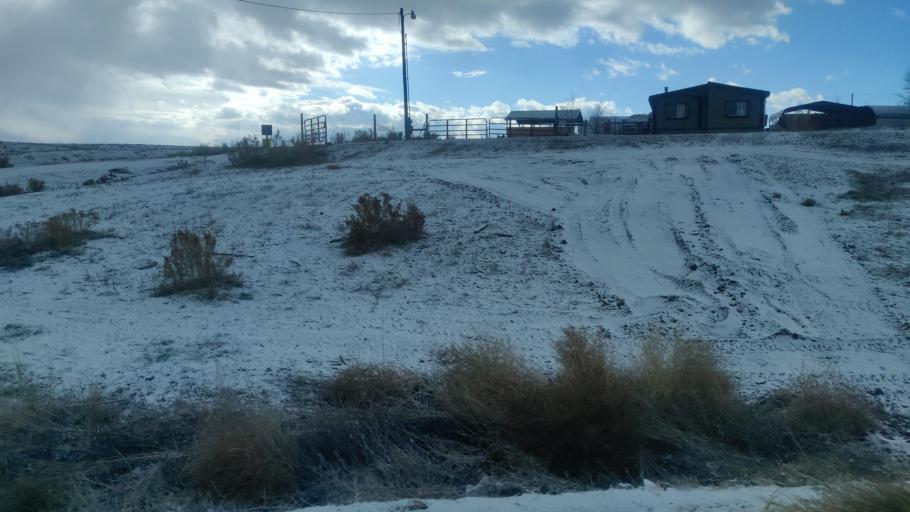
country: US
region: Colorado
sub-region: Mesa County
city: Clifton
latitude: 38.9892
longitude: -108.4415
